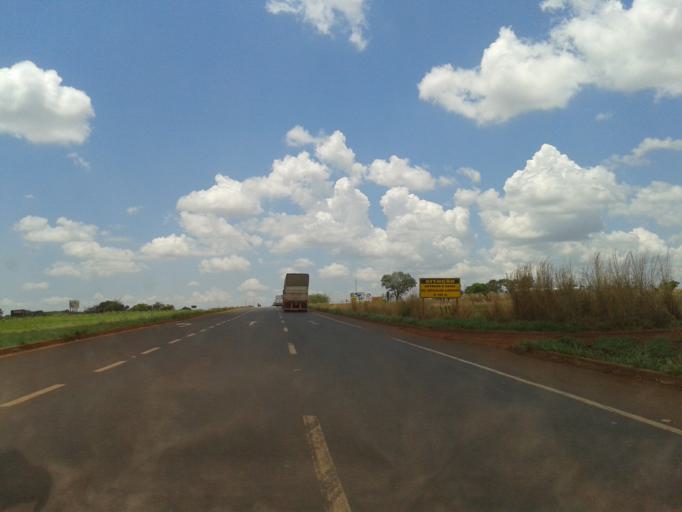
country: BR
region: Goias
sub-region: Itumbiara
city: Itumbiara
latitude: -18.3814
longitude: -49.3474
